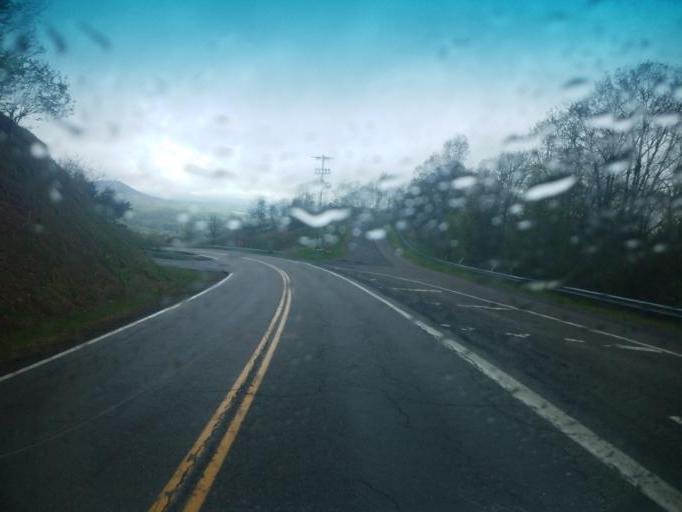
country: US
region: Virginia
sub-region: Smyth County
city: Adwolf
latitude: 36.7099
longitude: -81.6195
